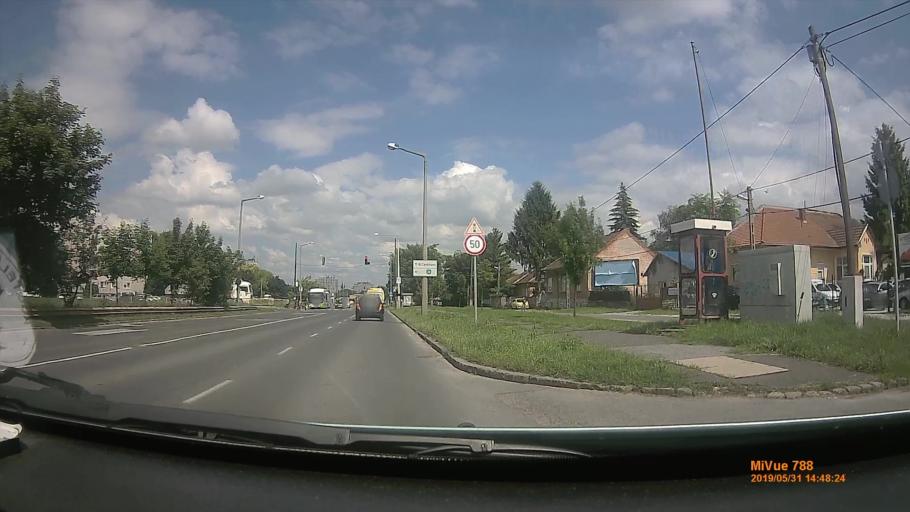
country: HU
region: Borsod-Abauj-Zemplen
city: Miskolc
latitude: 48.1014
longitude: 20.7569
